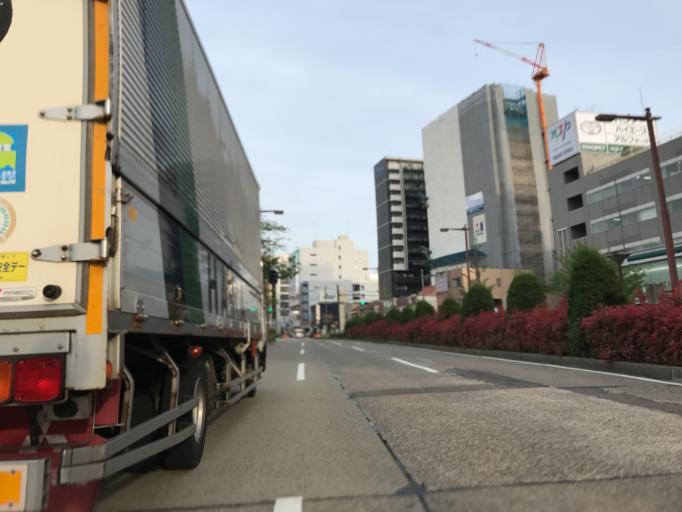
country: JP
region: Aichi
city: Nagoya-shi
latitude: 35.1720
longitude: 136.9350
